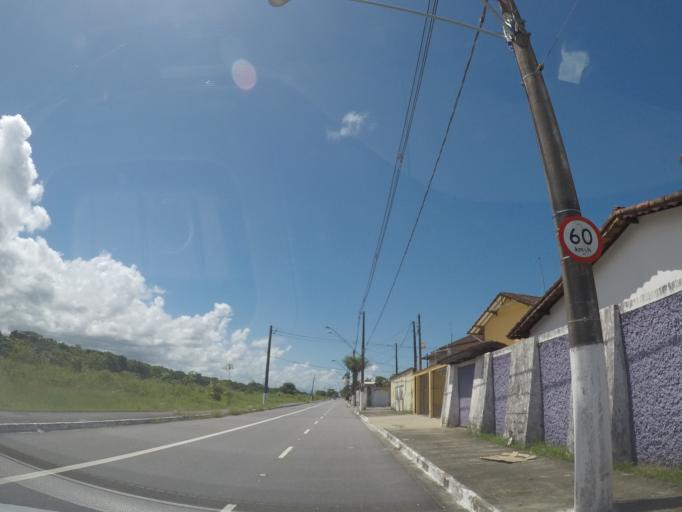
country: BR
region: Sao Paulo
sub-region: Mongagua
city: Mongagua
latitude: -24.0725
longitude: -46.5812
